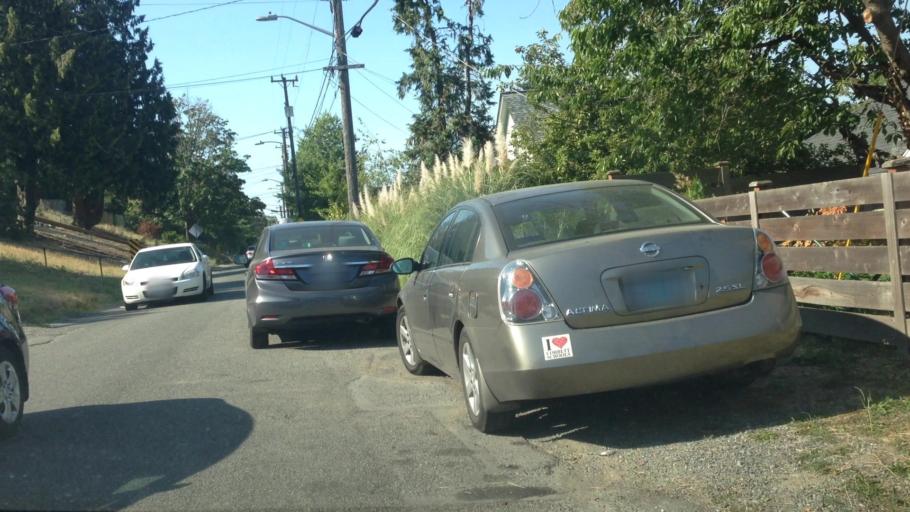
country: US
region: Washington
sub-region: King County
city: Seattle
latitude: 47.5629
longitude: -122.2890
